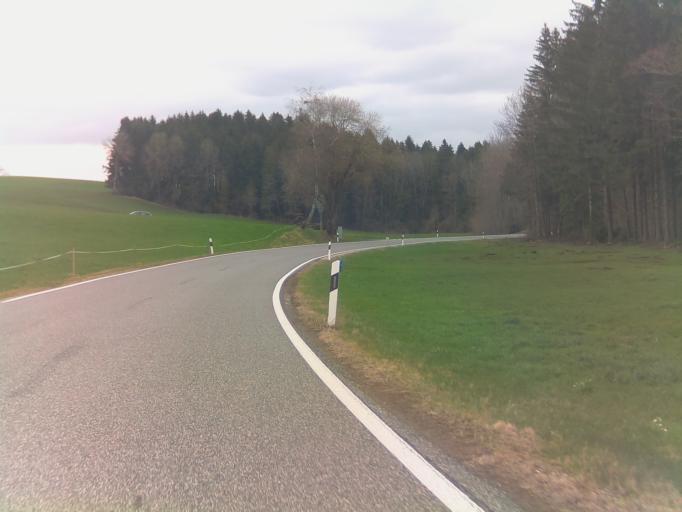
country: DE
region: Bavaria
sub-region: Upper Bavaria
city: Uffing
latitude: 47.7151
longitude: 11.1247
